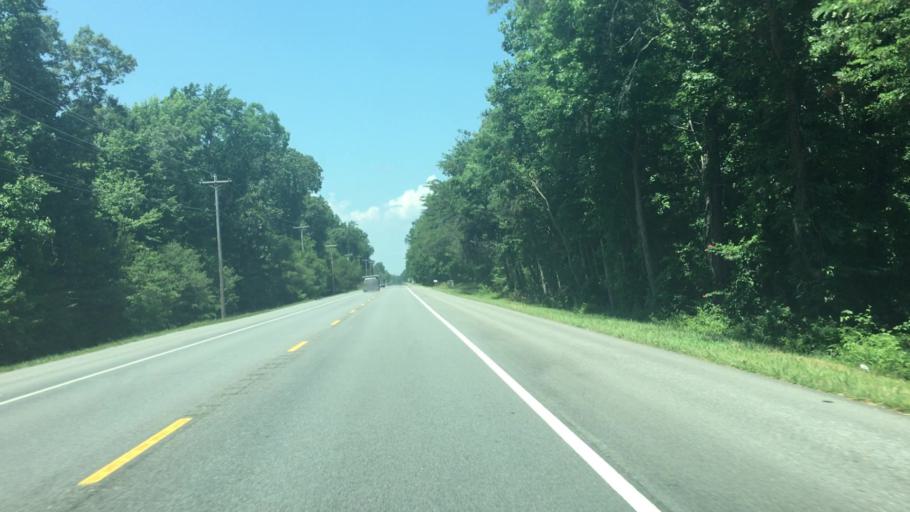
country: US
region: Maryland
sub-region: Saint Mary's County
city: Mechanicsville
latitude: 38.3873
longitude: -76.8222
